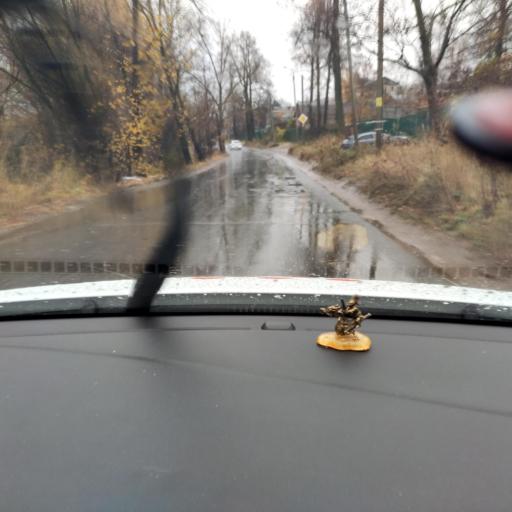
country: RU
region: Tatarstan
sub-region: Gorod Kazan'
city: Kazan
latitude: 55.7269
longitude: 49.1582
